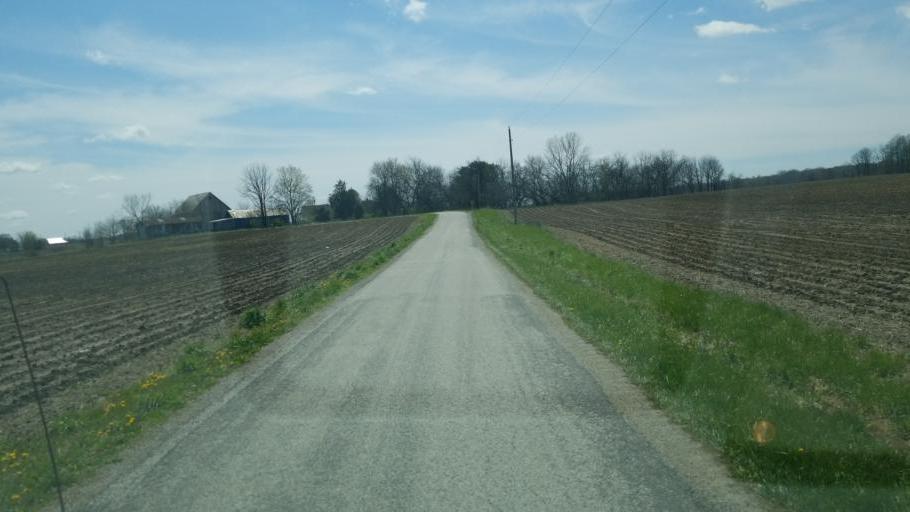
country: US
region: Ohio
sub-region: Union County
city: Richwood
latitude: 40.5128
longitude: -83.2899
